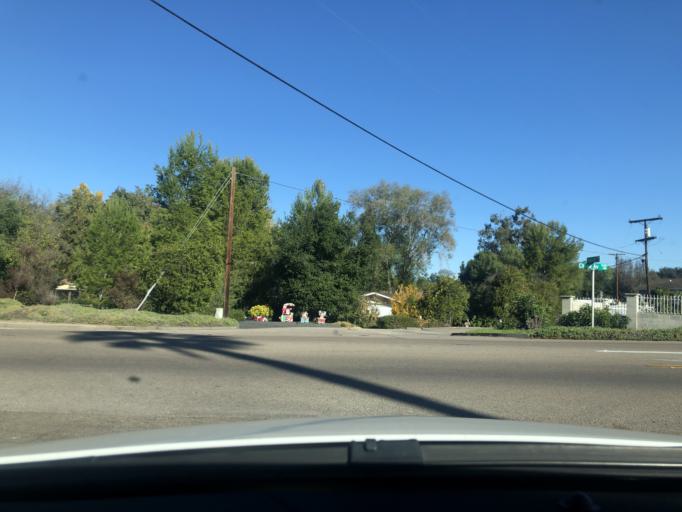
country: US
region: California
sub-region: San Diego County
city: Rancho San Diego
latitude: 32.7714
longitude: -116.9388
